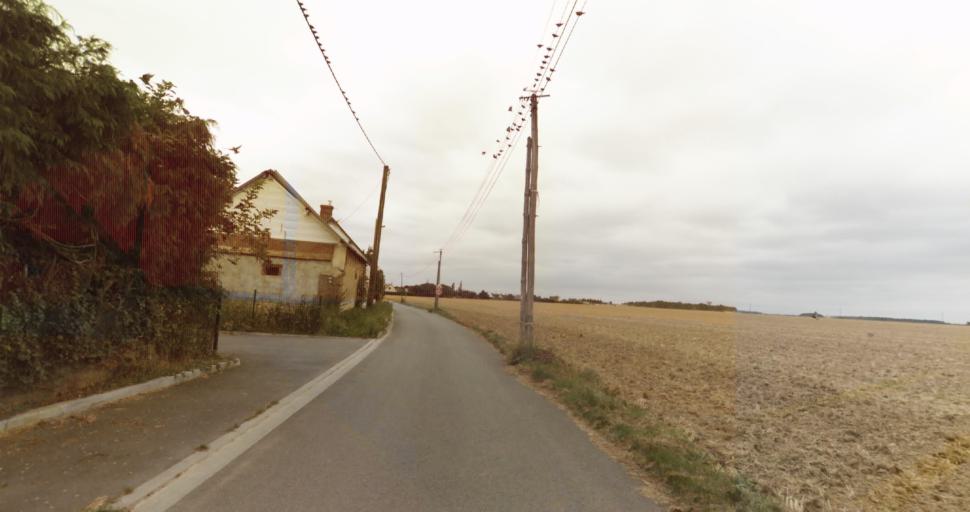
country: FR
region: Haute-Normandie
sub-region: Departement de l'Eure
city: Marcilly-sur-Eure
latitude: 48.9130
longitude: 1.3015
